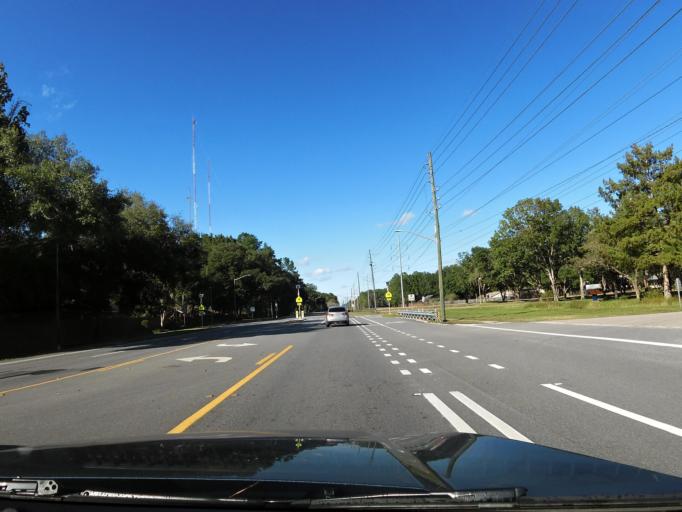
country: US
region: Florida
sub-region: Alachua County
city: Alachua
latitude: 29.7068
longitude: -82.3888
